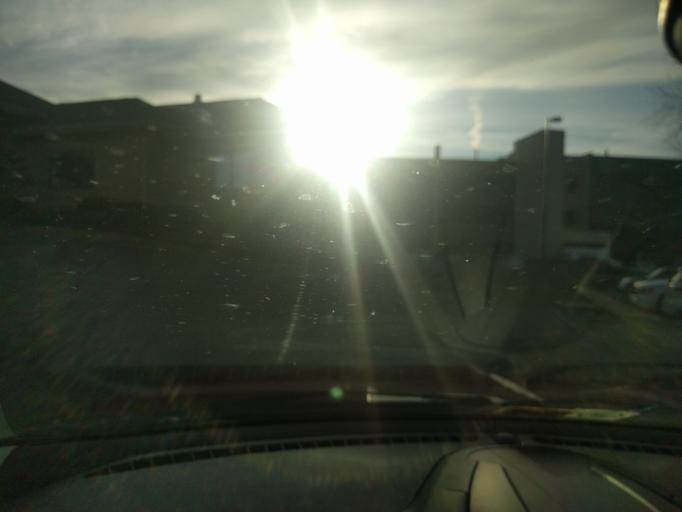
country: US
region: Virginia
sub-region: Augusta County
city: Fishersville
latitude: 38.0916
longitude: -78.9917
